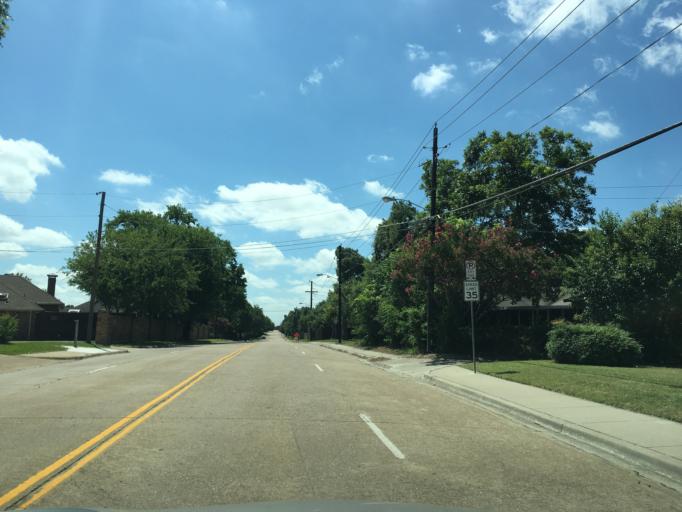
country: US
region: Texas
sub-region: Dallas County
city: Garland
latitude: 32.8432
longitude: -96.6548
